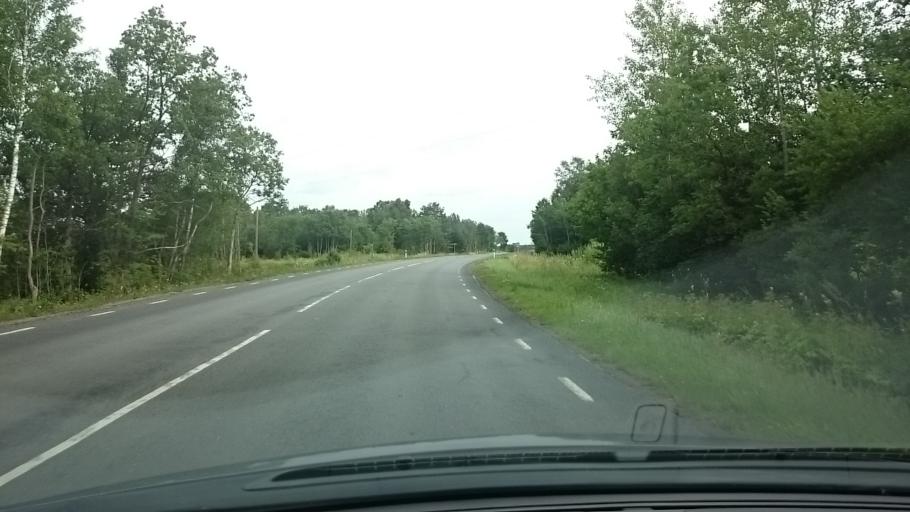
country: EE
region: Laeaene
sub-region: Ridala Parish
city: Uuemoisa
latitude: 58.9801
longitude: 23.6830
